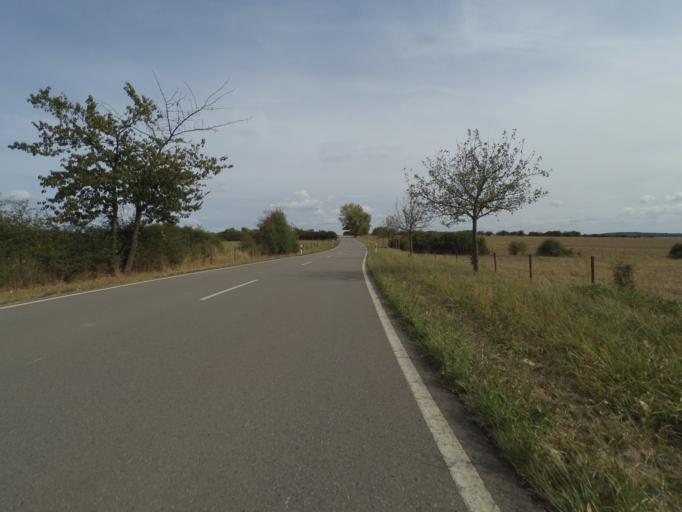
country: LU
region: Grevenmacher
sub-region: Canton de Remich
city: Mondorf-les-Bains
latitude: 49.4881
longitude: 6.3109
